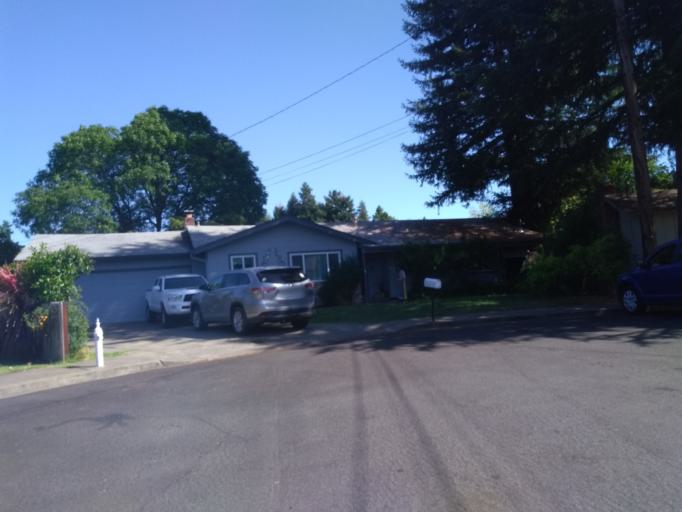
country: US
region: California
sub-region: Mendocino County
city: Ukiah
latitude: 39.1356
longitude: -123.2124
